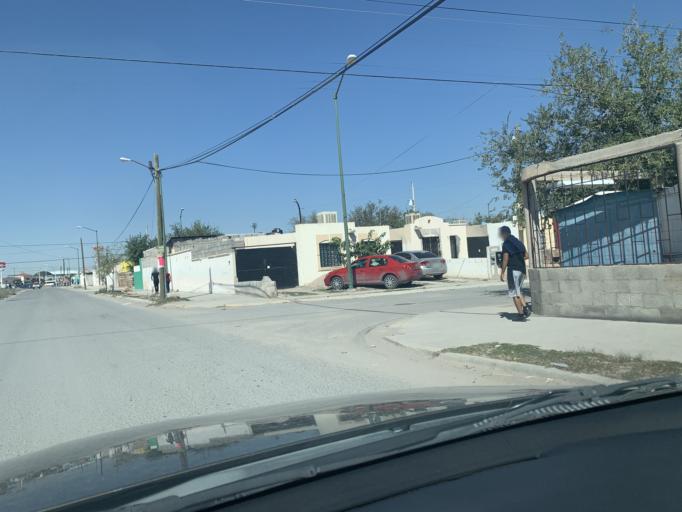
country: US
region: Texas
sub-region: El Paso County
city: Socorro Mission Number 1 Colonia
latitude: 31.5936
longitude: -106.3579
